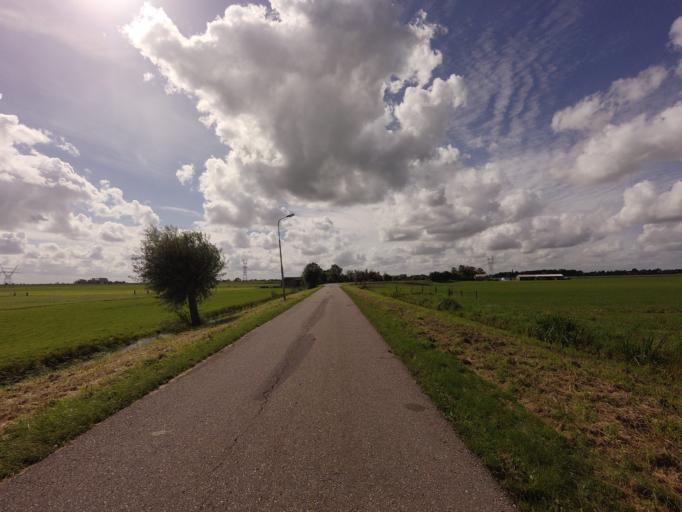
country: NL
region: North Holland
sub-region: Gemeente Waterland
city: Broek in Waterland
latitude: 52.4646
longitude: 4.9711
